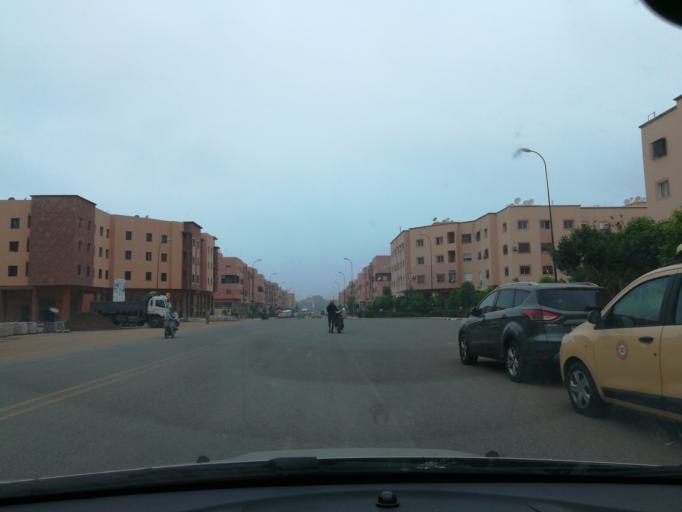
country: MA
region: Marrakech-Tensift-Al Haouz
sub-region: Marrakech
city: Marrakesh
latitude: 31.5745
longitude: -8.0575
